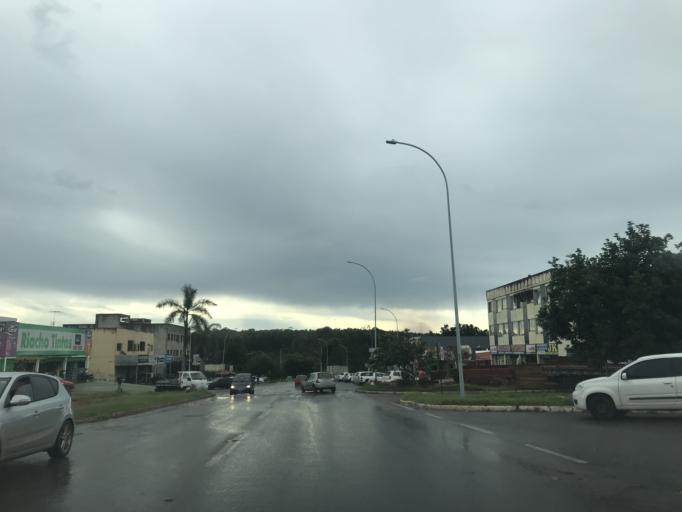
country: BR
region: Federal District
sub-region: Brasilia
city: Brasilia
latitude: -15.6421
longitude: -47.8075
